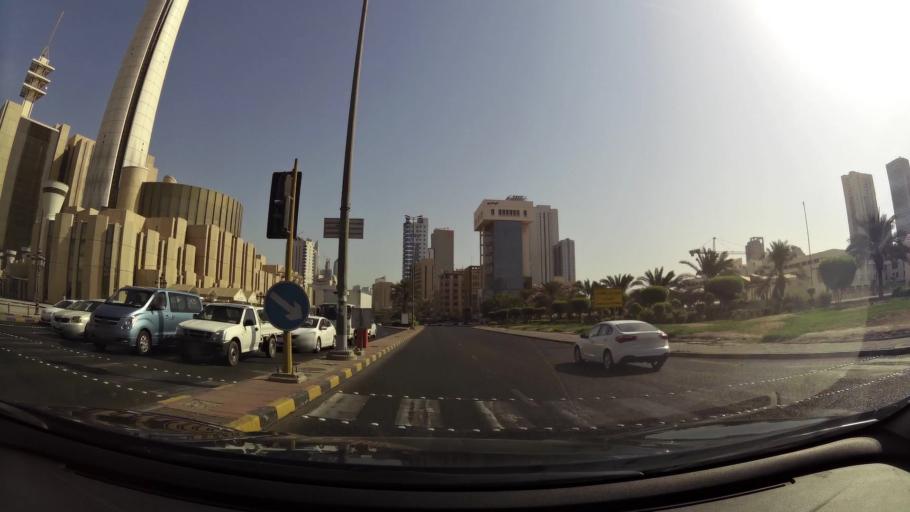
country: KW
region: Al Asimah
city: Kuwait City
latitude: 29.3671
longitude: 47.9744
